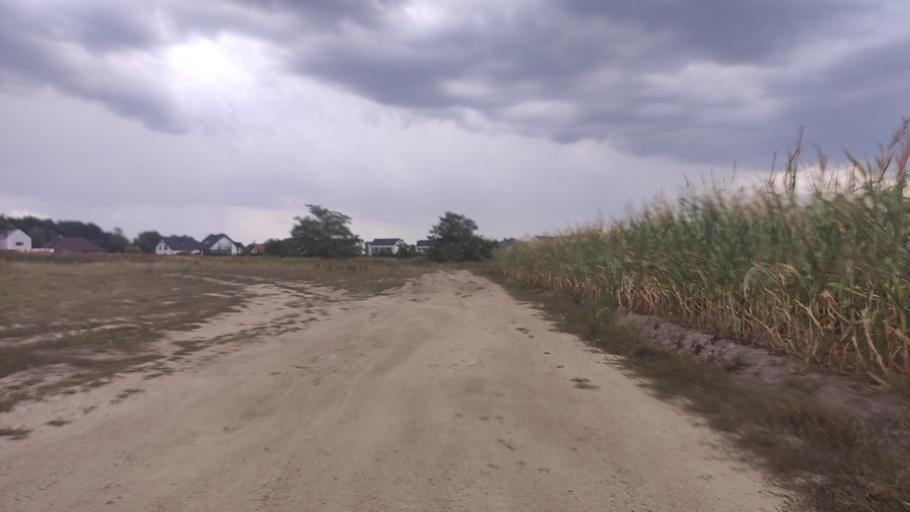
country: PL
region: Greater Poland Voivodeship
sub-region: Powiat poznanski
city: Swarzedz
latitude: 52.3933
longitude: 17.1235
